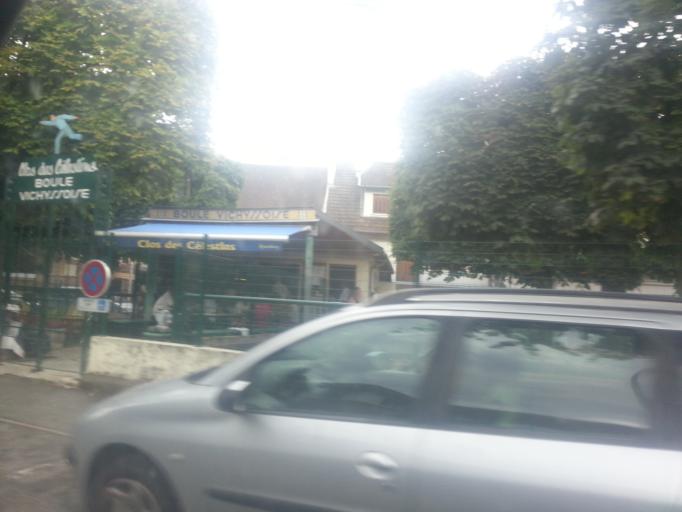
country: FR
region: Auvergne
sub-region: Departement de l'Allier
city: Vichy
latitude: 46.1190
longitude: 3.4254
